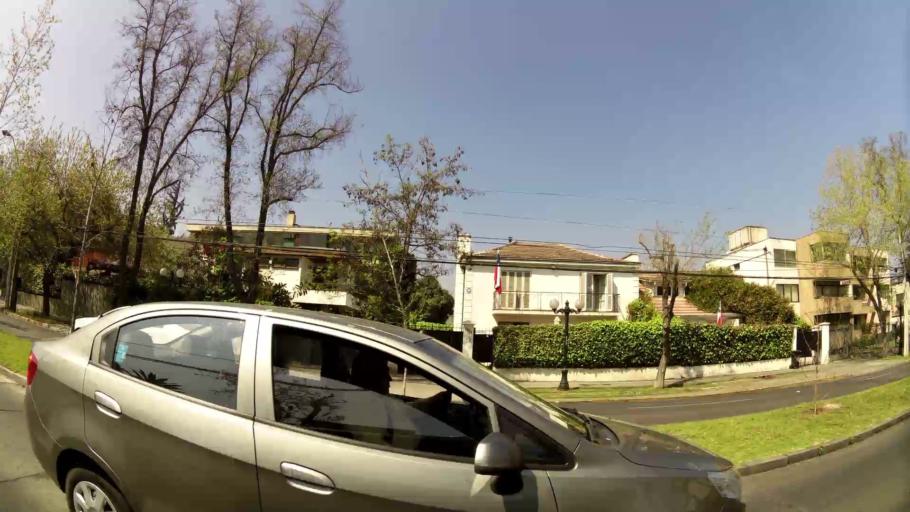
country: CL
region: Santiago Metropolitan
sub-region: Provincia de Santiago
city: Villa Presidente Frei, Nunoa, Santiago, Chile
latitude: -33.4377
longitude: -70.5910
